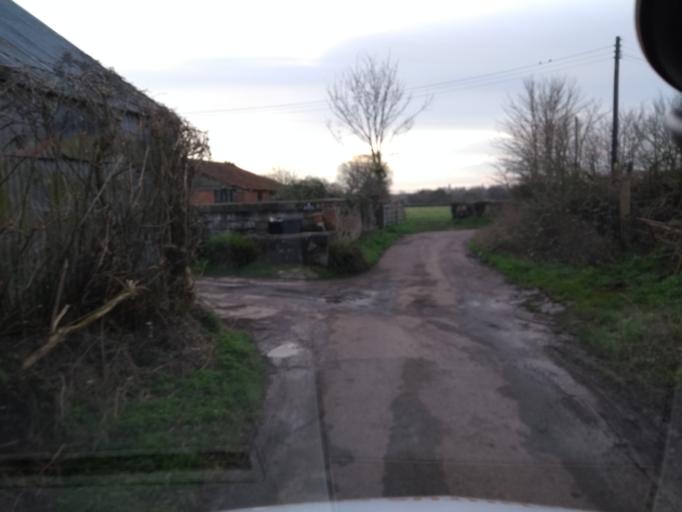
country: GB
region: England
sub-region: Somerset
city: Westonzoyland
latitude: 51.0923
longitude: -2.8909
